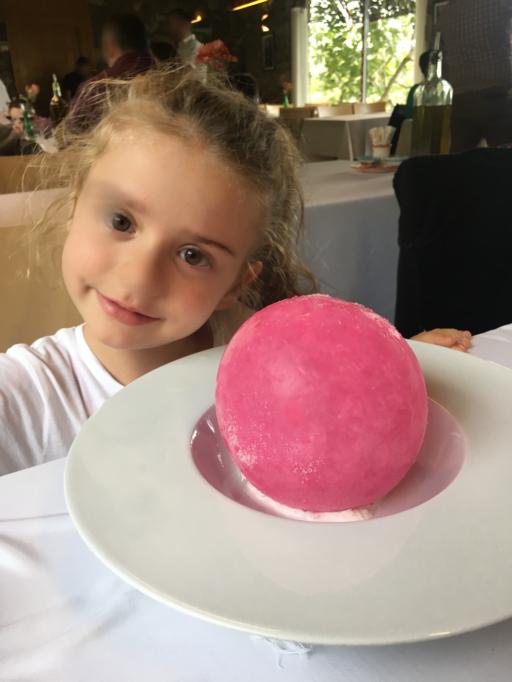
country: AL
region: Lezhe
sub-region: Rrethi i Lezhes
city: Kallmeti i Madh
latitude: 41.8995
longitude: 19.6723
